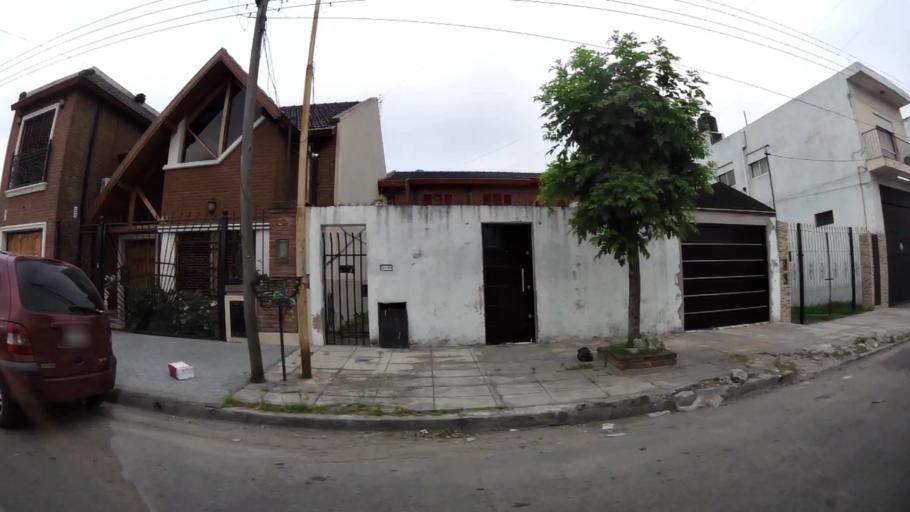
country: AR
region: Buenos Aires
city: San Justo
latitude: -34.6926
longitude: -58.5743
